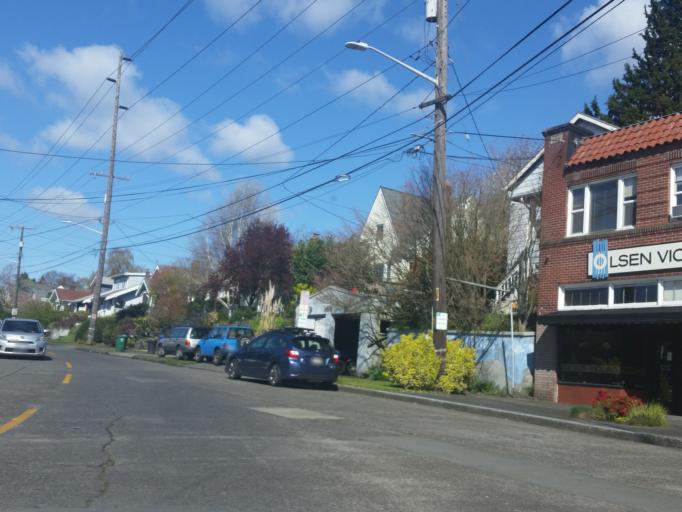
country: US
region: Washington
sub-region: King County
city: Seattle
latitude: 47.6761
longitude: -122.3606
